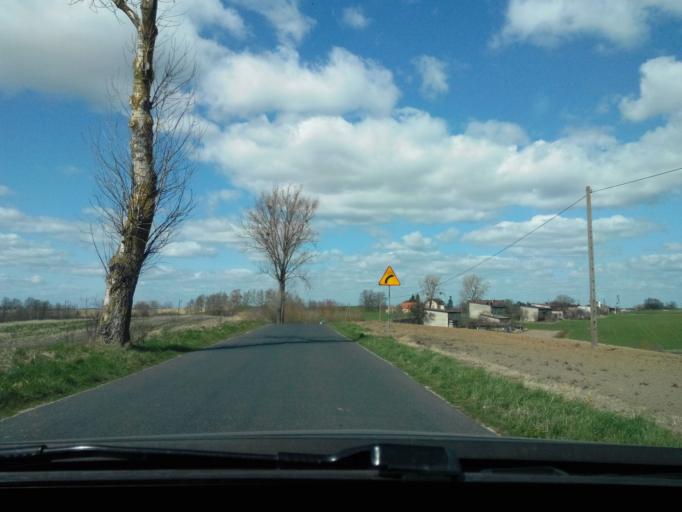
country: PL
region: Warmian-Masurian Voivodeship
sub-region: Powiat nowomiejski
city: Biskupiec
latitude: 53.4617
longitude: 19.3206
